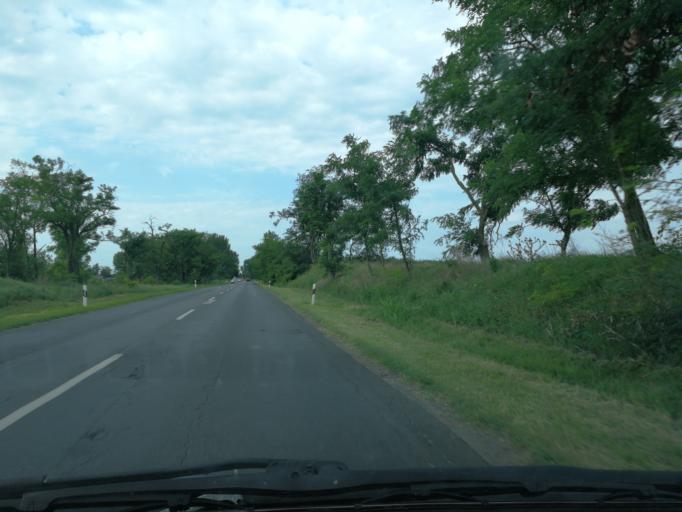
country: HU
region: Bacs-Kiskun
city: Ersekcsanad
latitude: 46.2219
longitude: 18.9657
